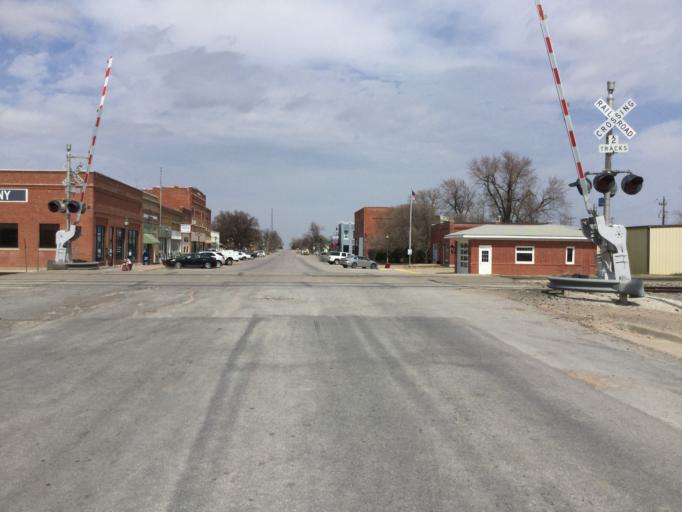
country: US
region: Kansas
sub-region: Kiowa County
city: Greensburg
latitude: 37.6150
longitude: -99.1062
